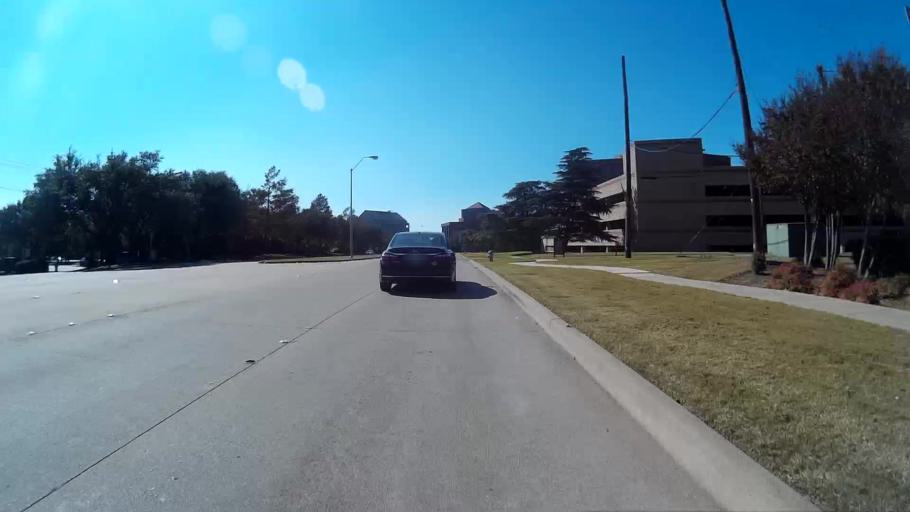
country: US
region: Texas
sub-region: Dallas County
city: Richardson
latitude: 32.9788
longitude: -96.7082
